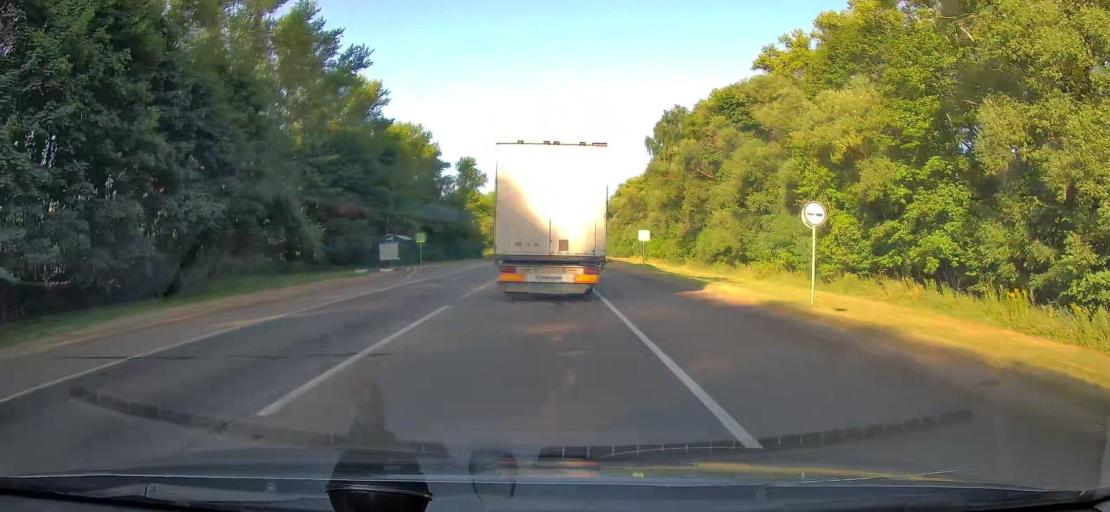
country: RU
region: Tula
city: Chern'
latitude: 53.4630
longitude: 36.9469
